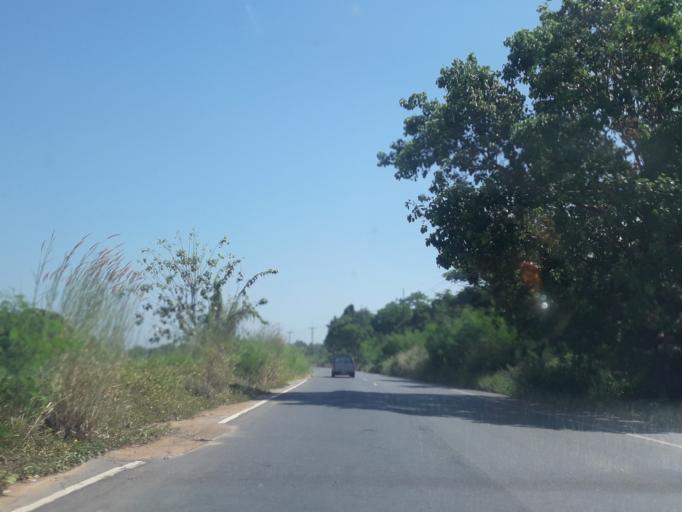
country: TH
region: Sara Buri
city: Nong Khae
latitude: 14.3032
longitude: 100.8465
